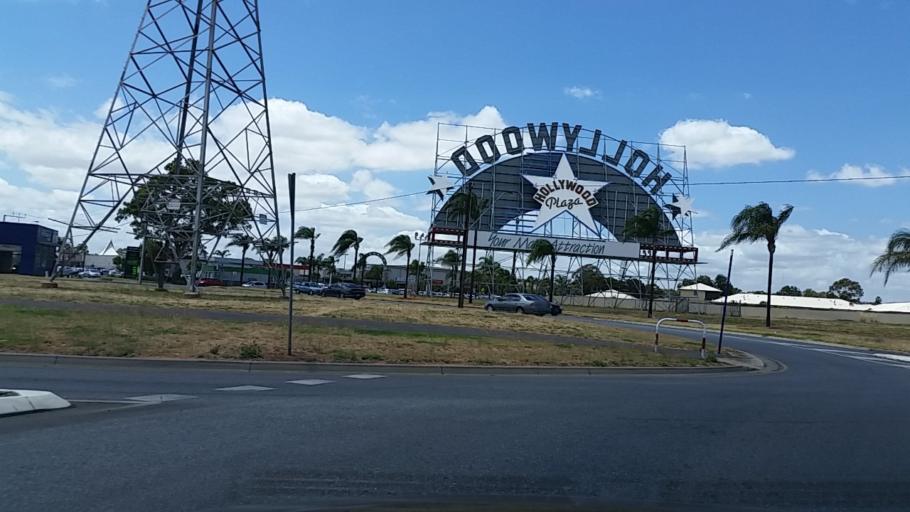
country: AU
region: South Australia
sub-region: Salisbury
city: Salisbury
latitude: -34.7679
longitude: 138.6210
